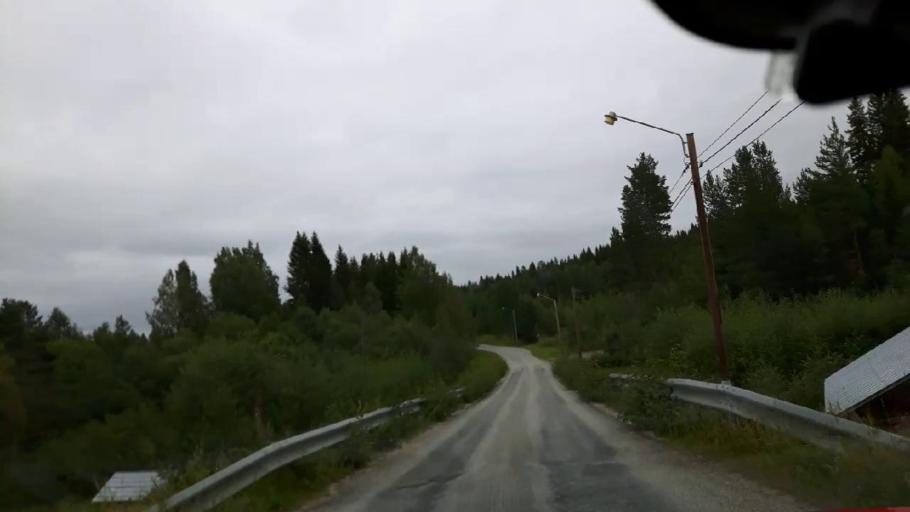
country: SE
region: Vaesternorrland
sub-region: Ange Kommun
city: Fransta
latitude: 62.7740
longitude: 15.9901
